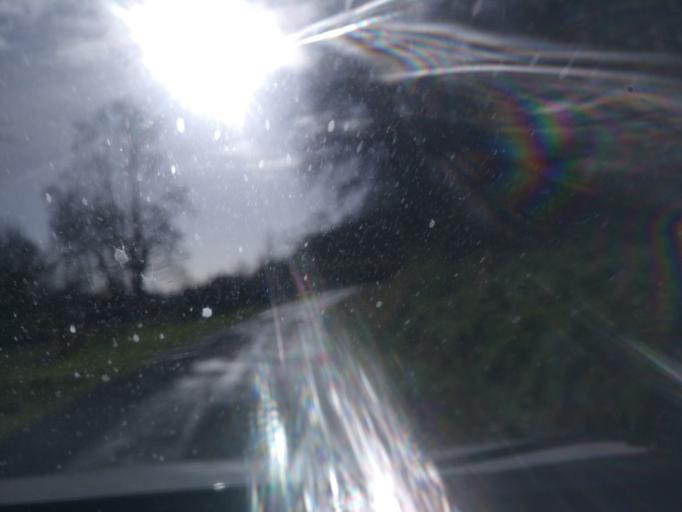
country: FR
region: Brittany
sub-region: Departement d'Ille-et-Vilaine
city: Antrain
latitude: 48.4992
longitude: -1.4994
